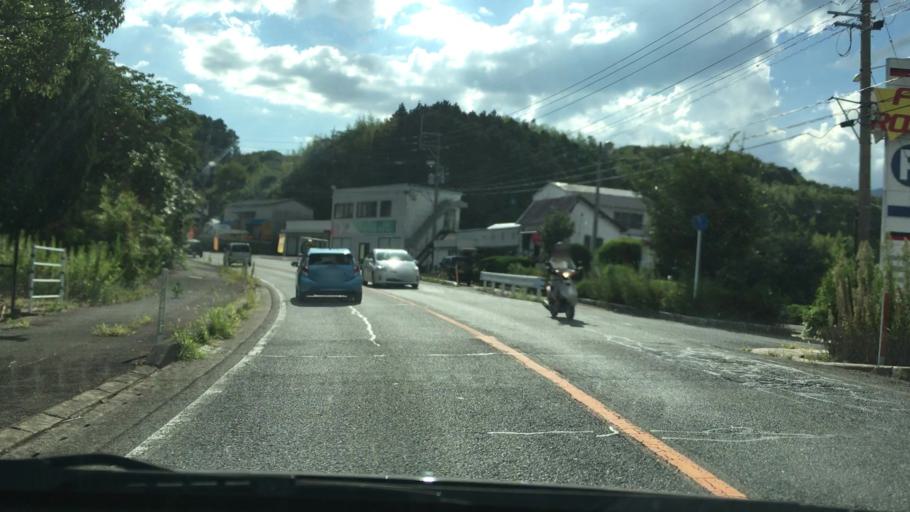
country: JP
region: Saga Prefecture
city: Imaricho-ko
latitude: 33.1893
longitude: 129.8615
